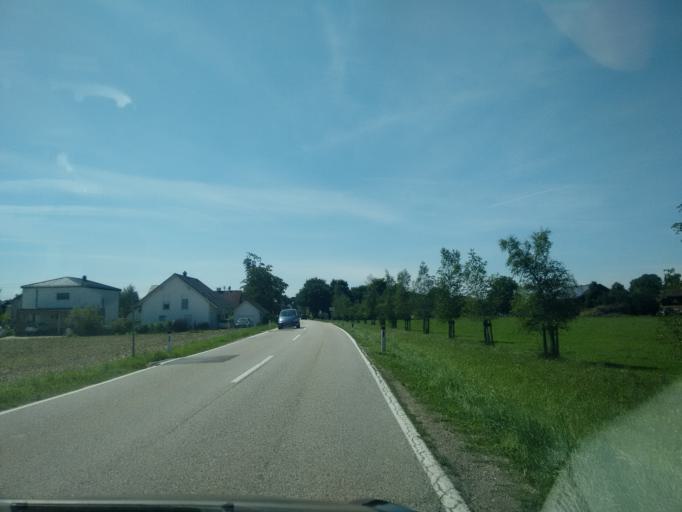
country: DE
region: Bavaria
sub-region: Lower Bavaria
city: Simbach am Inn
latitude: 48.2384
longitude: 13.0177
